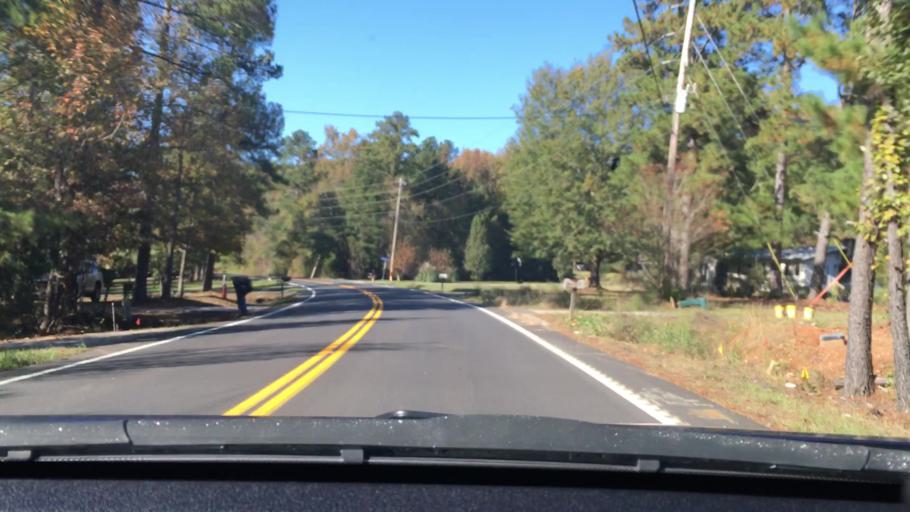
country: US
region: South Carolina
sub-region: Lexington County
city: Irmo
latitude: 34.1235
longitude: -81.1729
